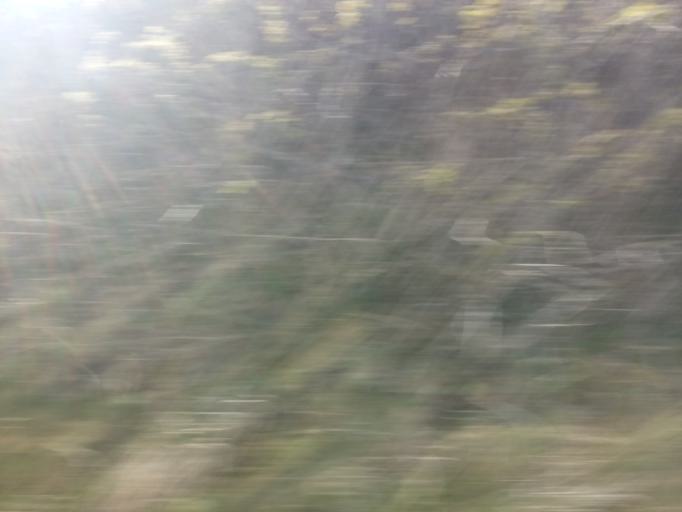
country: GB
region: Scotland
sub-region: The Scottish Borders
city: Eyemouth
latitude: 55.8427
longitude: -2.0981
